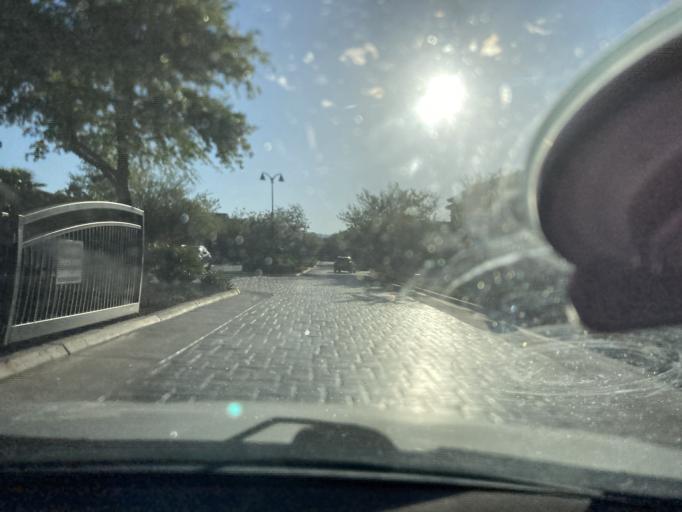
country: US
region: Nevada
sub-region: Clark County
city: Summerlin South
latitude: 36.1574
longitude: -115.3450
